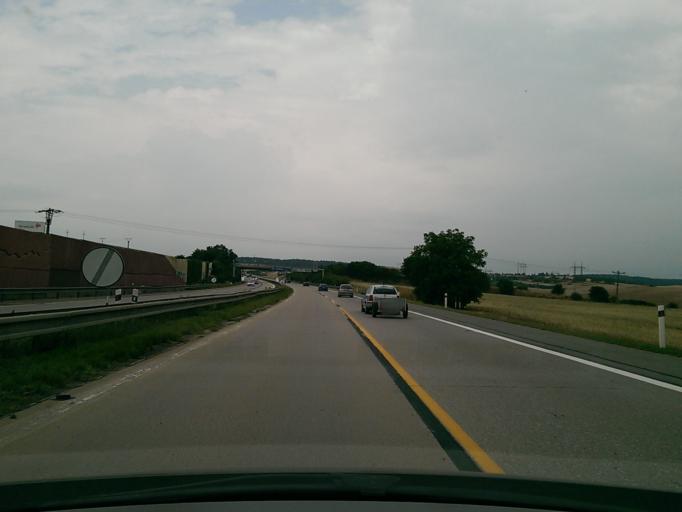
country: CZ
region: South Moravian
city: Ricany
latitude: 49.2183
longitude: 16.4068
